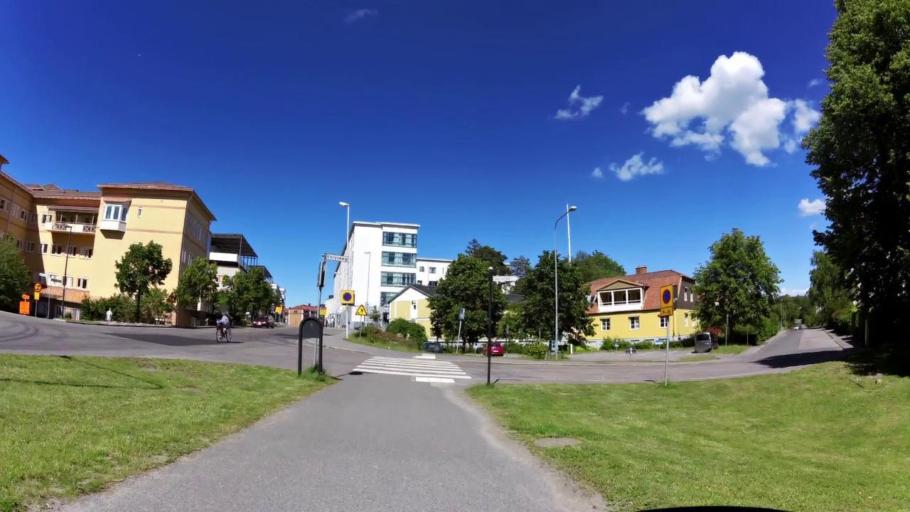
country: SE
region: OEstergoetland
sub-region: Linkopings Kommun
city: Linkoping
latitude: 58.3994
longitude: 15.6210
